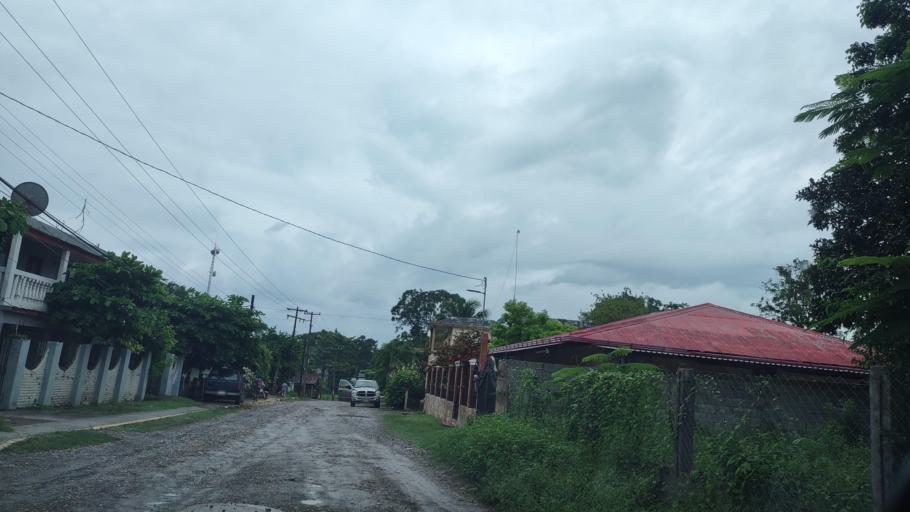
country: MX
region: San Luis Potosi
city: Tanquian de Escobedo
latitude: 21.5452
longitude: -98.5530
